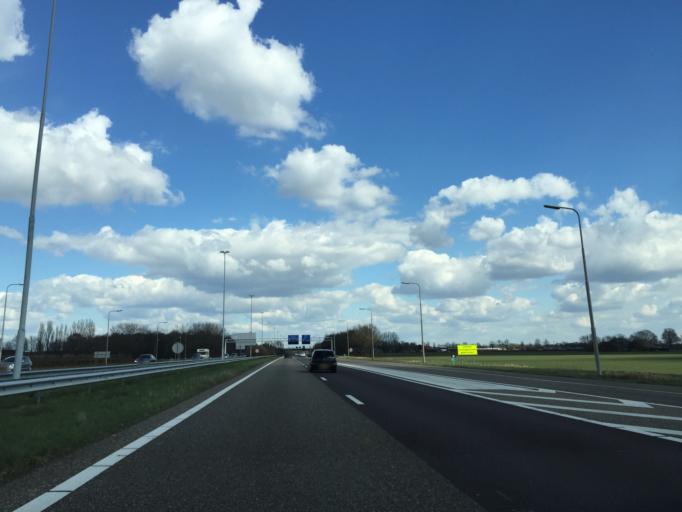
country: NL
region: North Brabant
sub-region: Gemeente Breda
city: Hoge Vucht
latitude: 51.5545
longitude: 4.8433
